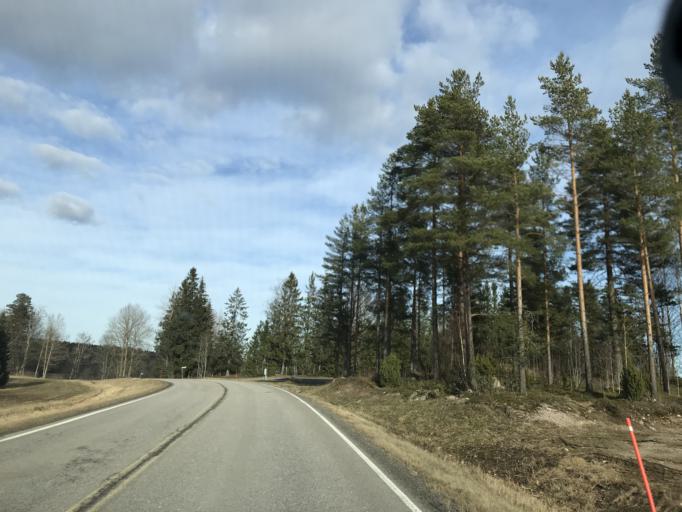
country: FI
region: Uusimaa
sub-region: Raaseporin
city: Ekenaes
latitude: 60.0831
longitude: 23.4087
